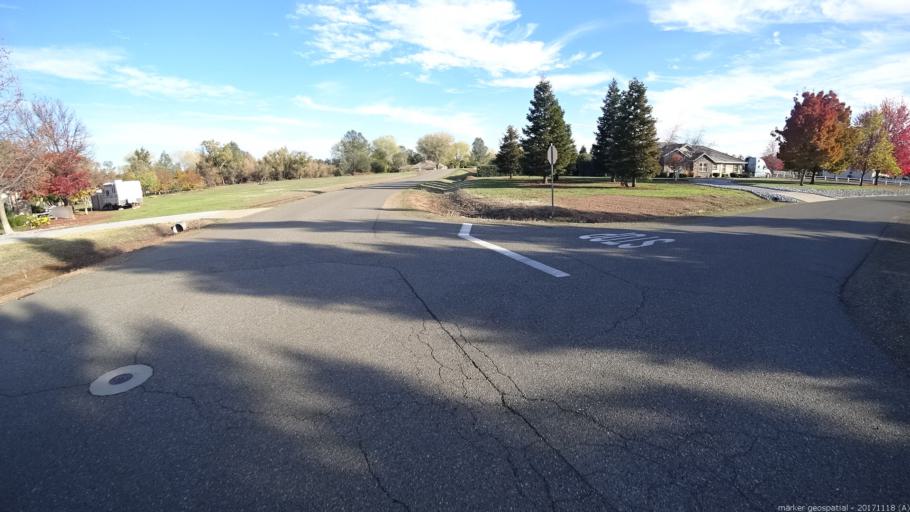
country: US
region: California
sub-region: Shasta County
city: Cottonwood
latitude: 40.3782
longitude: -122.3351
